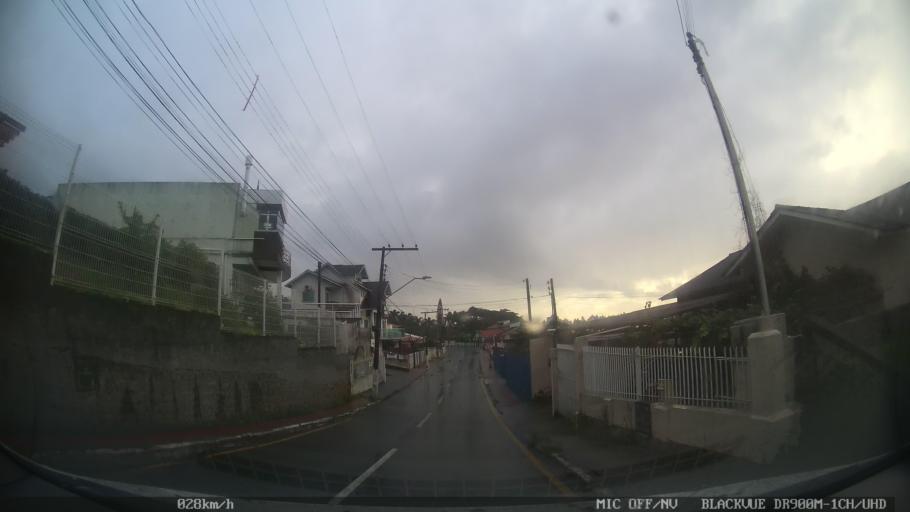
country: BR
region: Santa Catarina
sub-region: Sao Jose
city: Campinas
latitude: -27.6138
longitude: -48.6259
